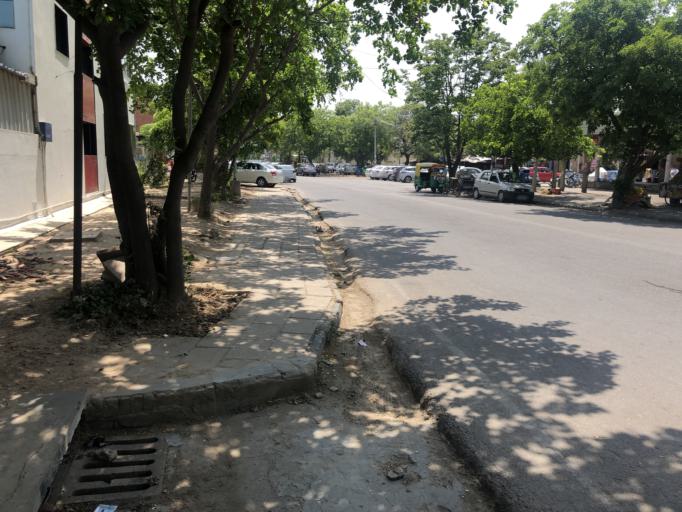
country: IN
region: Chandigarh
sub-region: Chandigarh
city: Chandigarh
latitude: 30.7110
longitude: 76.7543
